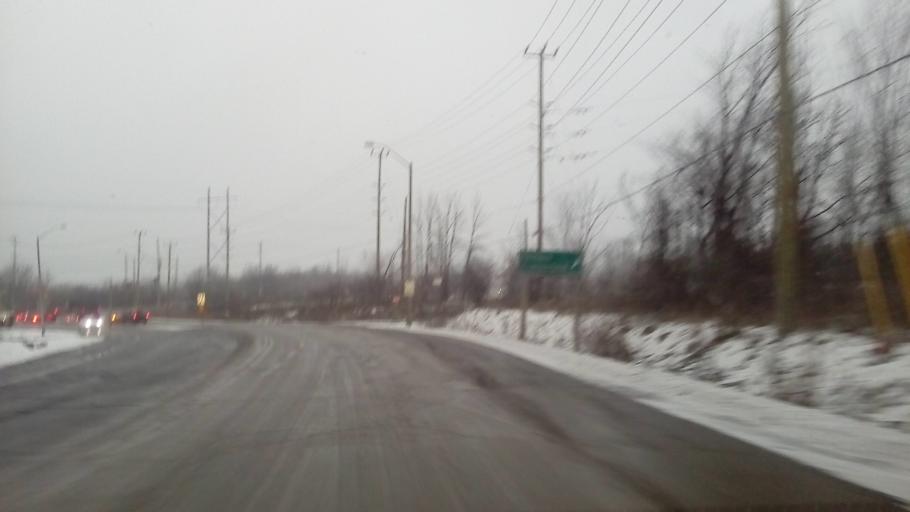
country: CA
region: Quebec
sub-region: Outaouais
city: Gatineau
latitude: 45.4516
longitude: -75.5754
